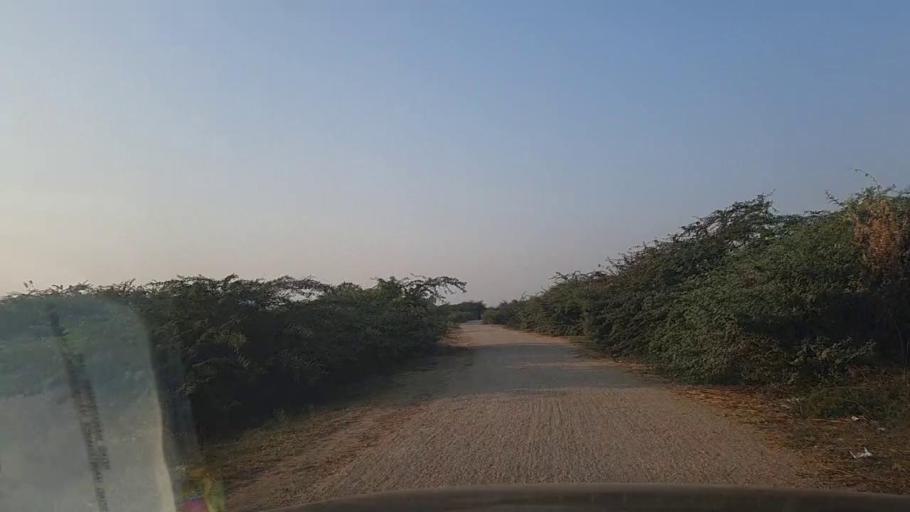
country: PK
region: Sindh
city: Keti Bandar
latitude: 24.3091
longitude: 67.6019
